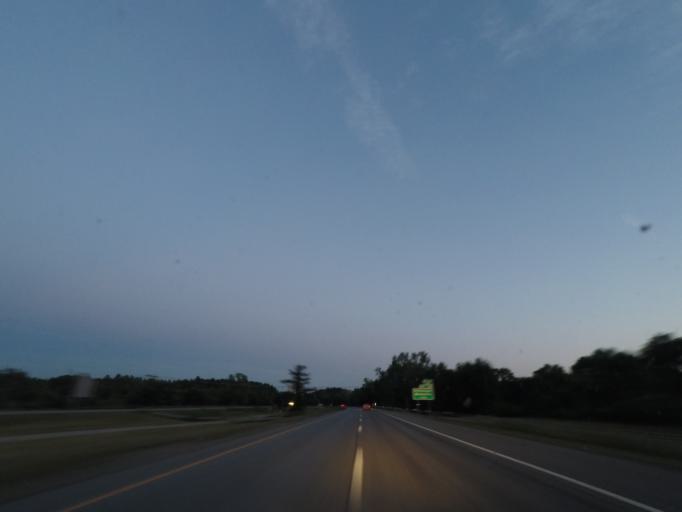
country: US
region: Connecticut
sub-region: Windham County
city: Putnam
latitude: 41.8857
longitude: -71.8967
